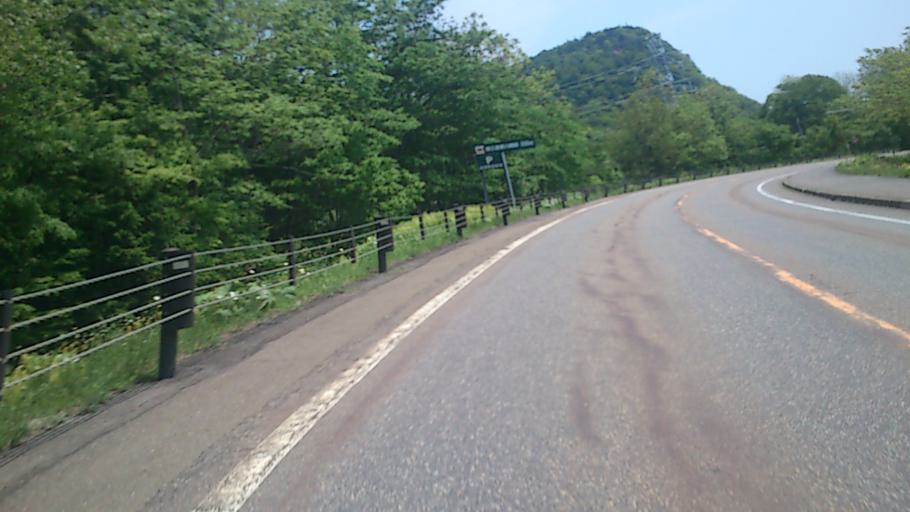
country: JP
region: Hokkaido
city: Otofuke
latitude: 43.3599
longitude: 143.2527
